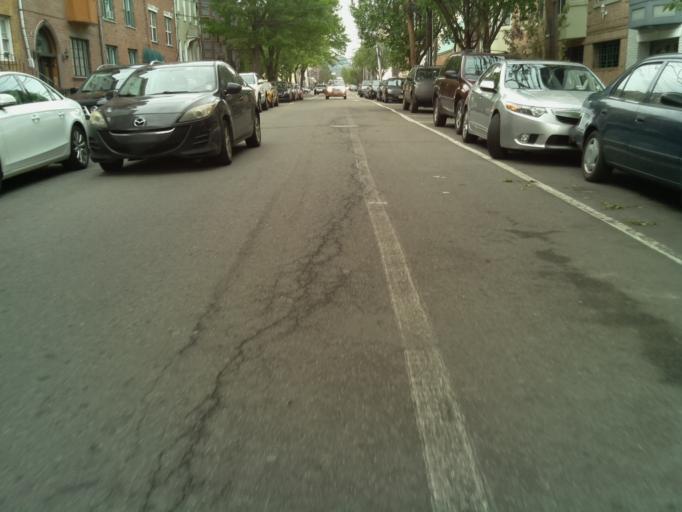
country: US
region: New Jersey
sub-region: Hudson County
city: Hoboken
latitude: 40.7449
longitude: -74.0364
